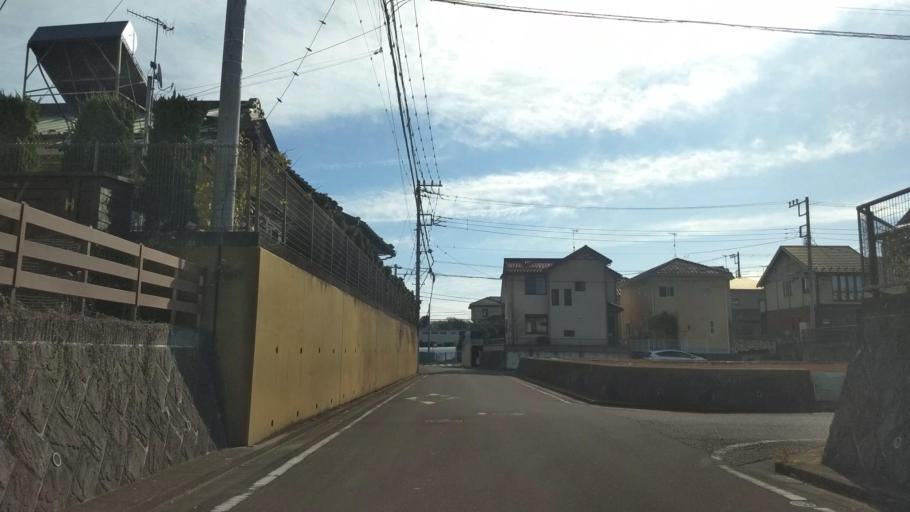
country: JP
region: Kanagawa
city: Hadano
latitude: 35.3600
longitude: 139.2336
